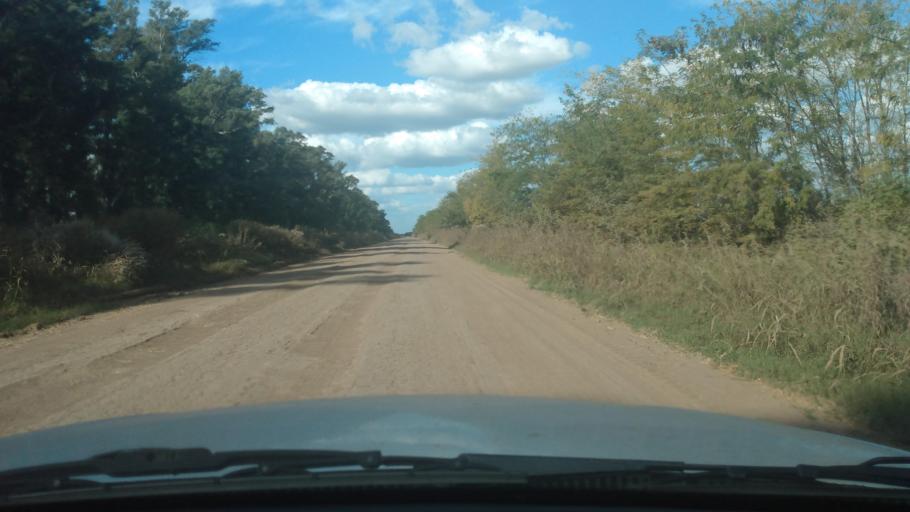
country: AR
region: Buenos Aires
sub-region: Partido de Navarro
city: Navarro
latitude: -35.0121
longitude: -59.5054
